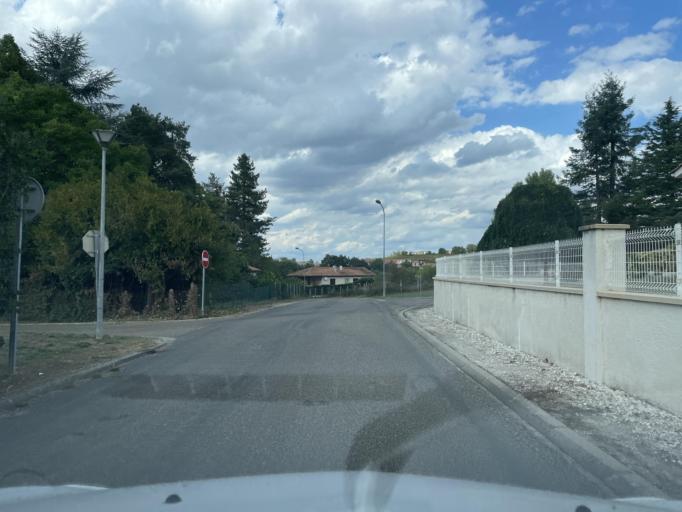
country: FR
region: Aquitaine
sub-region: Departement du Lot-et-Garonne
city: Casteljaloux
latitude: 44.3101
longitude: 0.0963
